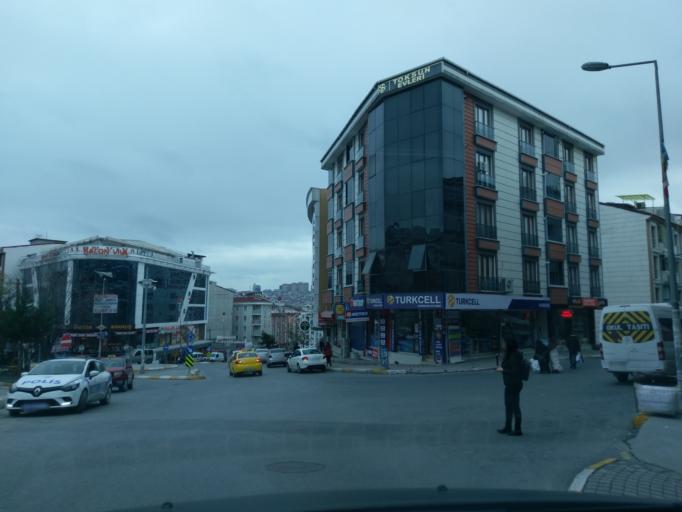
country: TR
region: Istanbul
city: Esenyurt
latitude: 41.0177
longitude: 28.6648
